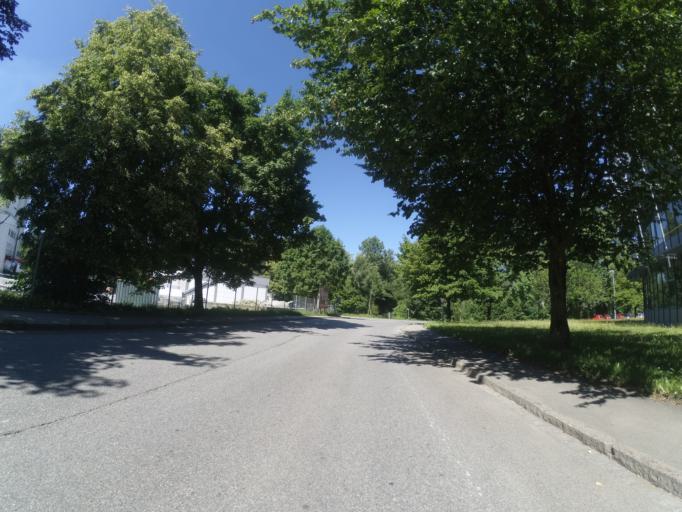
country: DE
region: Baden-Wuerttemberg
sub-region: Tuebingen Region
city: Leutkirch im Allgau
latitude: 47.8347
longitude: 10.0127
